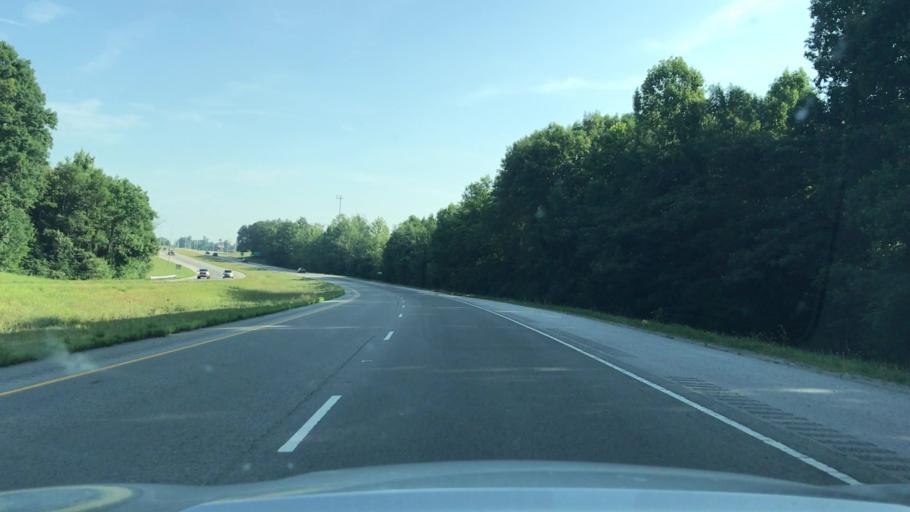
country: US
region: Tennessee
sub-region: Putnam County
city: Algood
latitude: 36.1720
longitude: -85.4610
